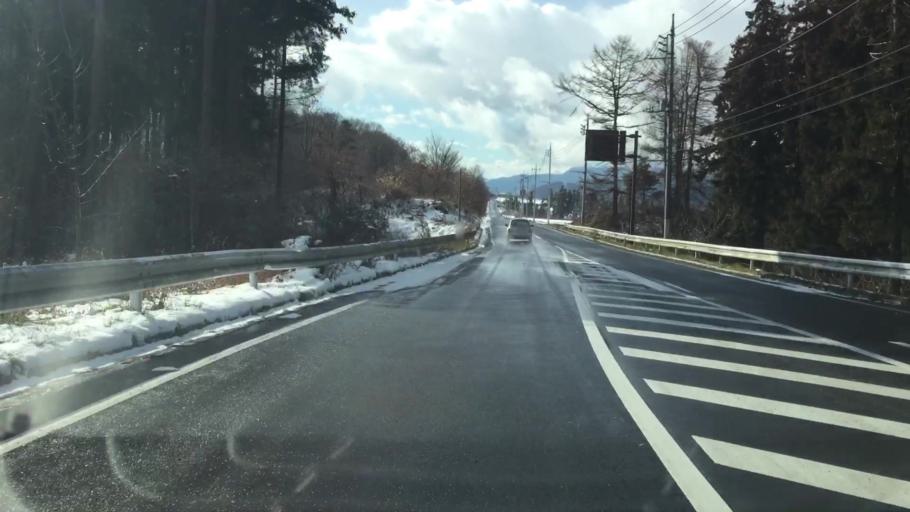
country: JP
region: Gunma
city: Numata
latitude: 36.6221
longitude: 139.0881
